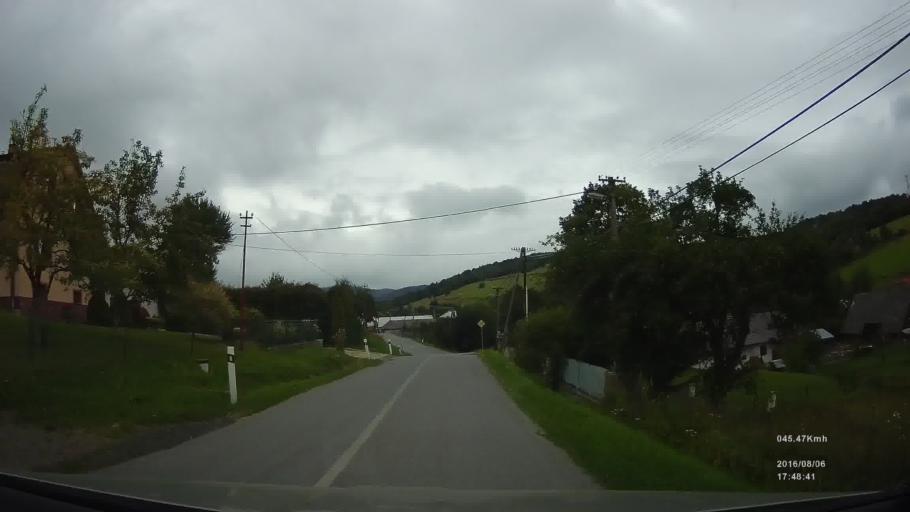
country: SK
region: Presovsky
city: Svidnik
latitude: 49.3785
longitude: 21.5727
